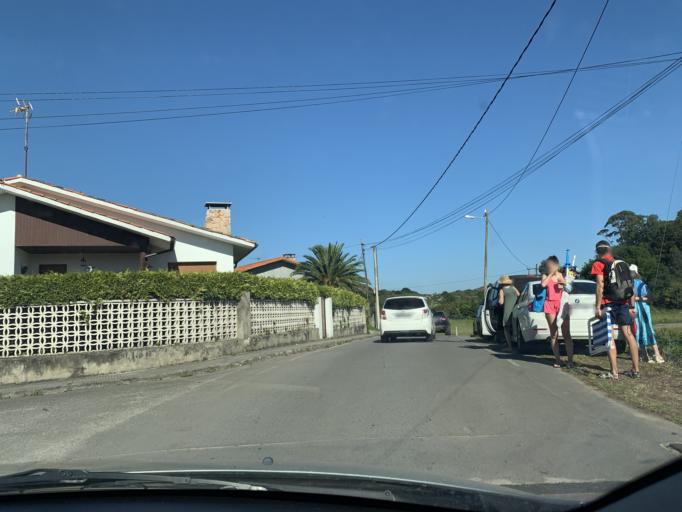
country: ES
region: Asturias
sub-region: Province of Asturias
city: Llanes
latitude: 43.4265
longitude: -4.7819
